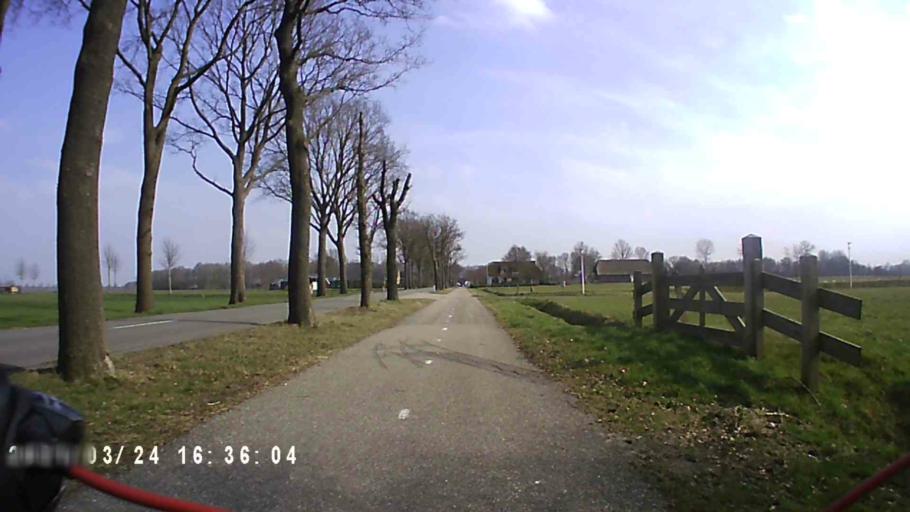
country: NL
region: Groningen
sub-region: Gemeente Leek
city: Leek
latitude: 53.0650
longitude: 6.2771
